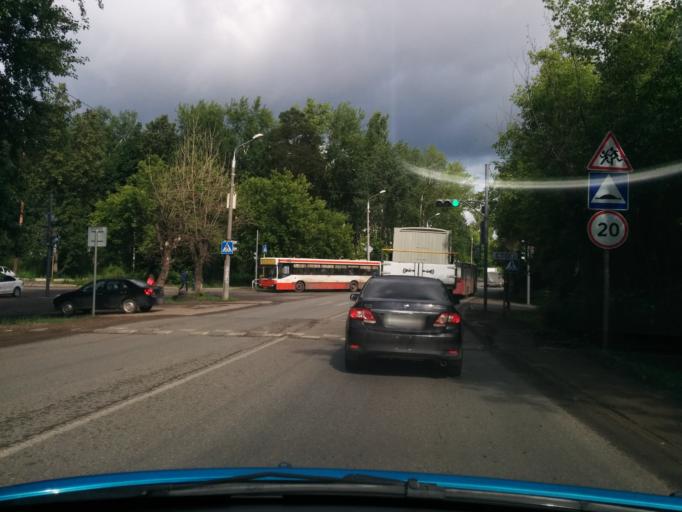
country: RU
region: Perm
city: Kondratovo
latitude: 58.0449
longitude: 56.0920
